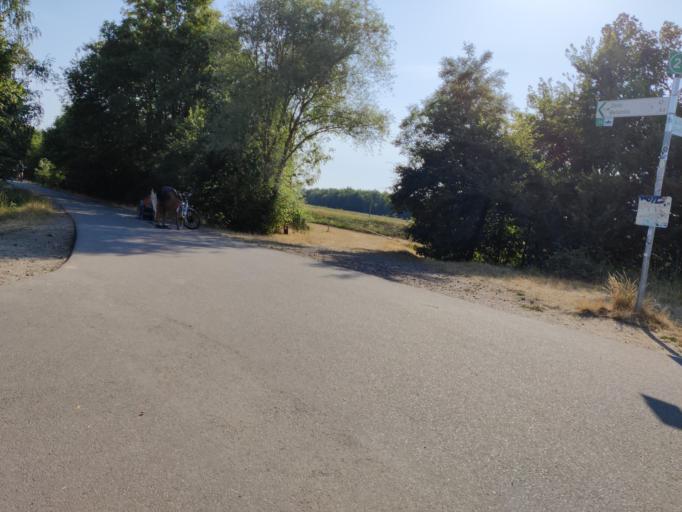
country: DE
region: Saxony
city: Markkleeberg
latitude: 51.2856
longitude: 12.3361
